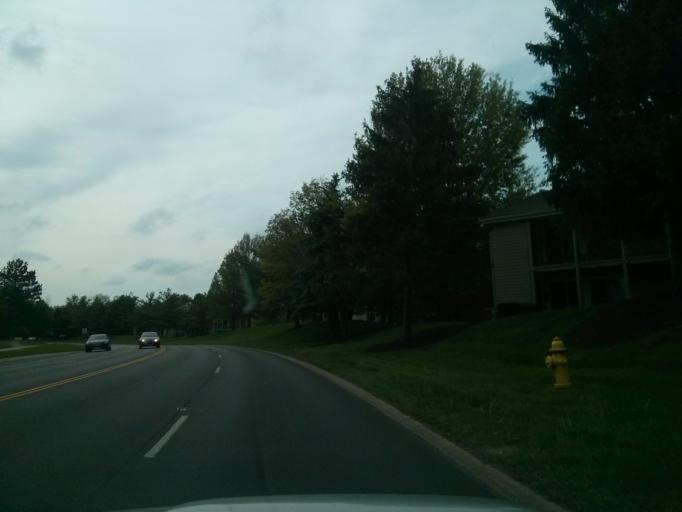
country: US
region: Indiana
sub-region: Hamilton County
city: Carmel
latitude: 39.9690
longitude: -86.1471
